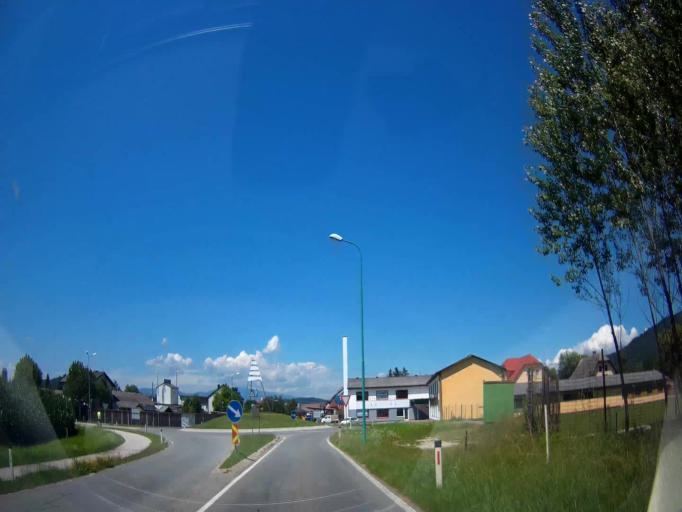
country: AT
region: Carinthia
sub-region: Politischer Bezirk Volkermarkt
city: Bleiburg/Pliberk
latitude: 46.5992
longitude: 14.7971
